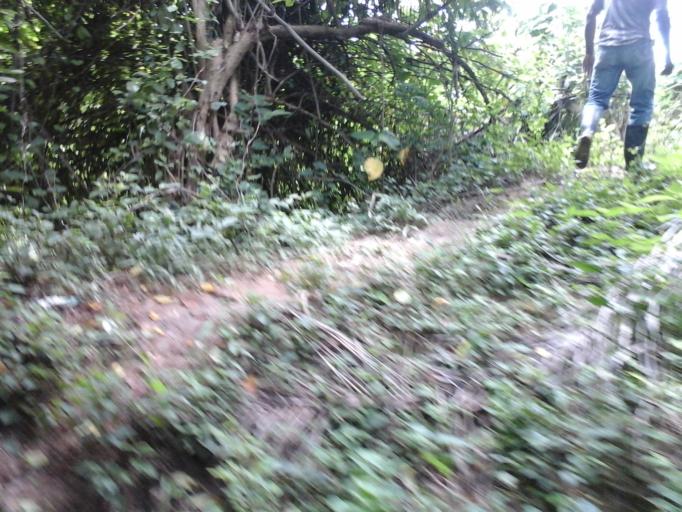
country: CO
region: Bolivar
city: San Pablo
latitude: 10.1574
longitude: -75.2743
